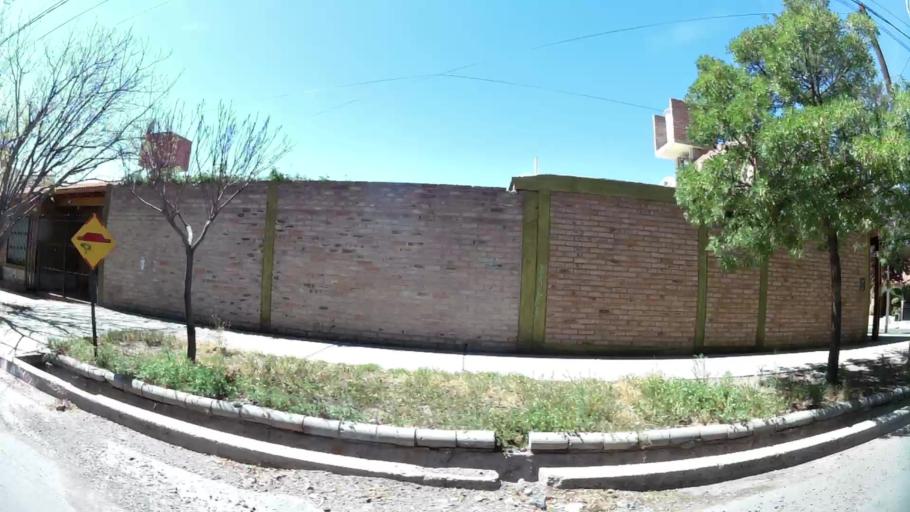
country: AR
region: Mendoza
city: Las Heras
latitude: -32.8412
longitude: -68.8735
